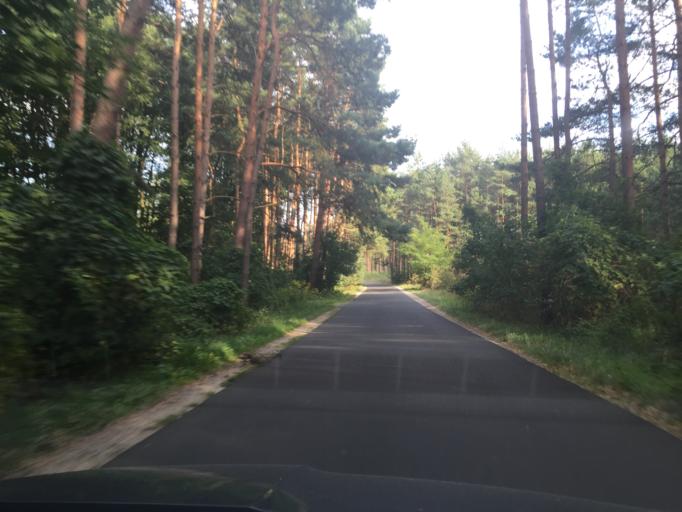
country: DE
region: Brandenburg
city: Grunheide
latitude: 52.3581
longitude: 13.7990
